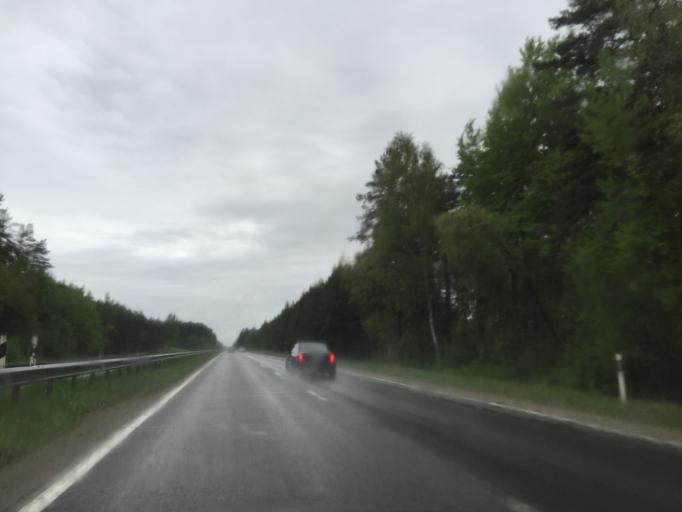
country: LV
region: Ikskile
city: Ikskile
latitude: 56.8269
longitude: 24.5238
